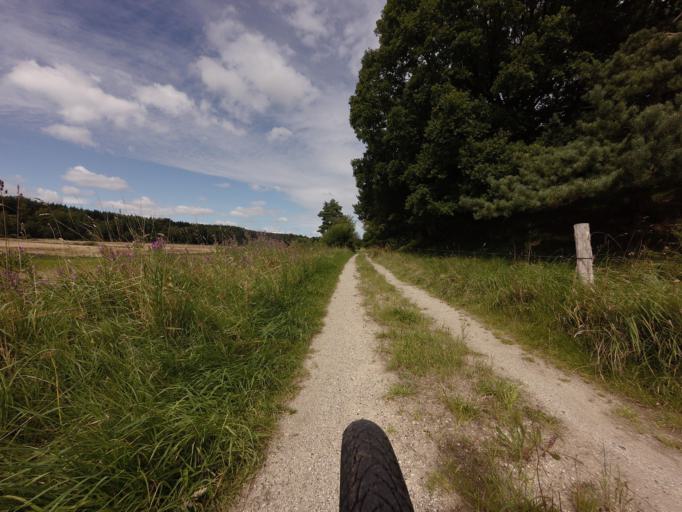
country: DK
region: Central Jutland
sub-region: Syddjurs Kommune
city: Ryomgard
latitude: 56.3920
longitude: 10.5319
